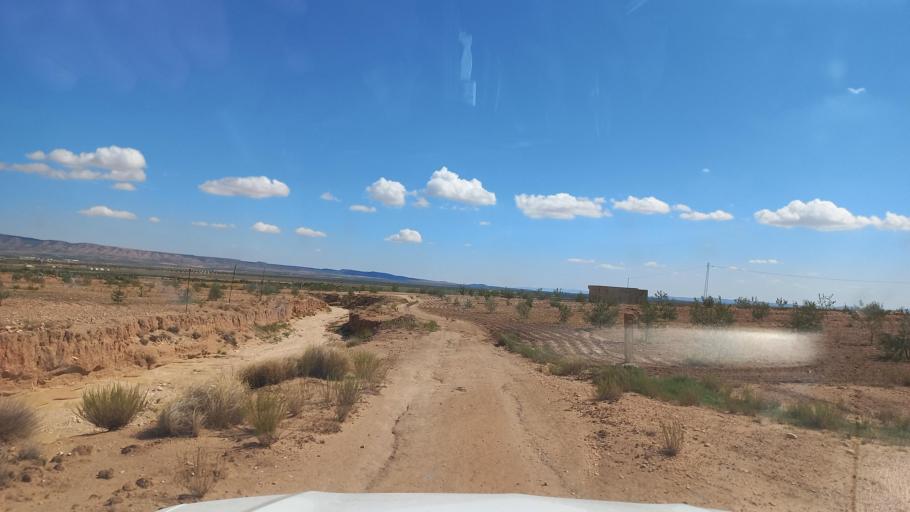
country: TN
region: Al Qasrayn
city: Sbiba
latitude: 35.3536
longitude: 9.0176
